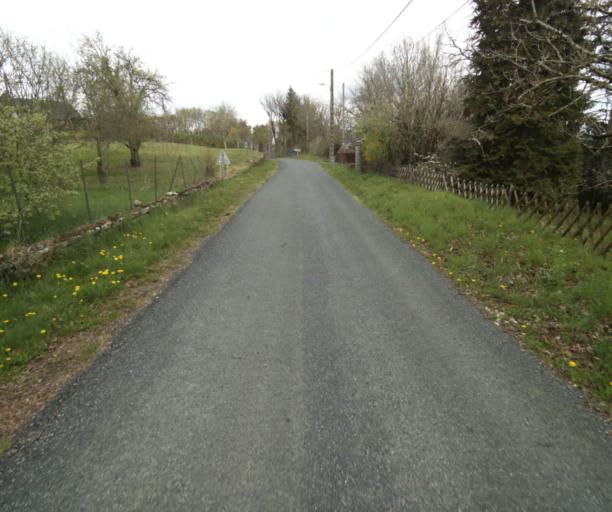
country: FR
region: Limousin
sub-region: Departement de la Correze
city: Sainte-Fortunade
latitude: 45.1909
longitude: 1.8629
